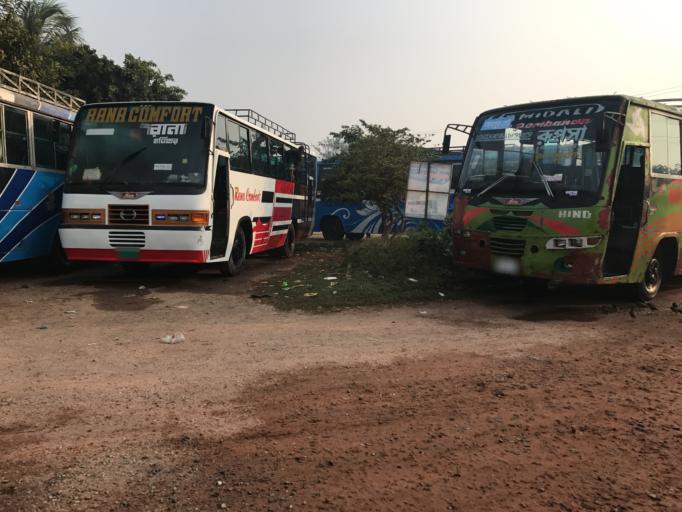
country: BD
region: Khulna
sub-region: Magura
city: Magura
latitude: 23.4970
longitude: 89.4322
